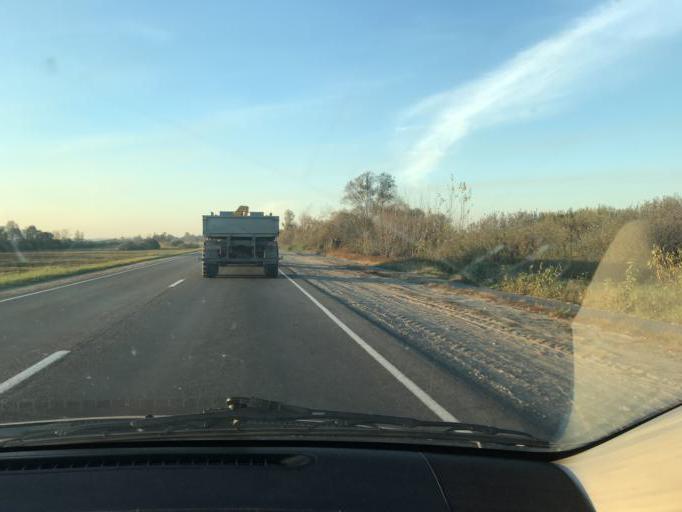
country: BY
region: Brest
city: Pinsk
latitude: 52.0775
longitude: 26.1457
